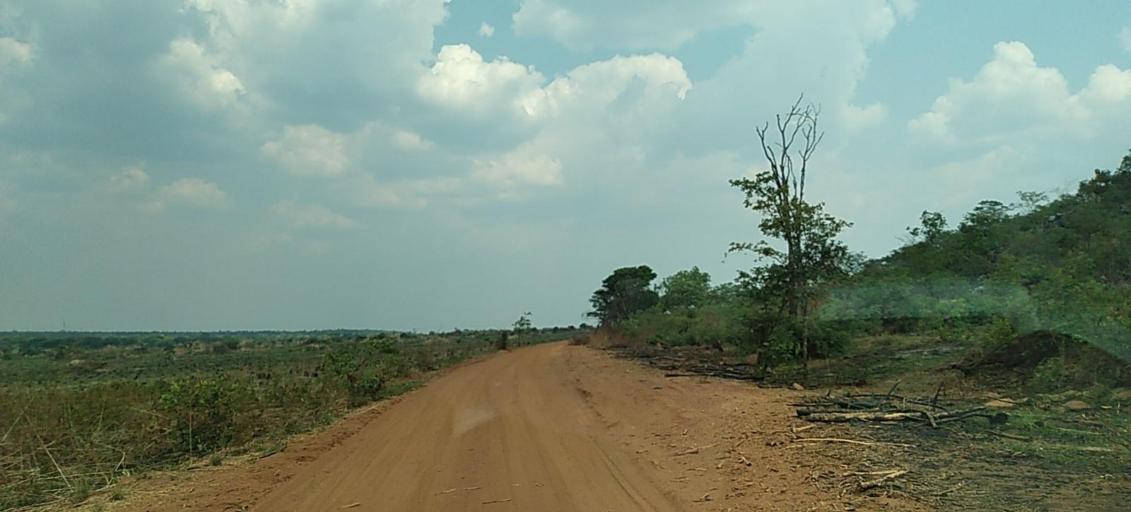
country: ZM
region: Copperbelt
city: Chingola
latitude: -12.7415
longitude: 27.7746
